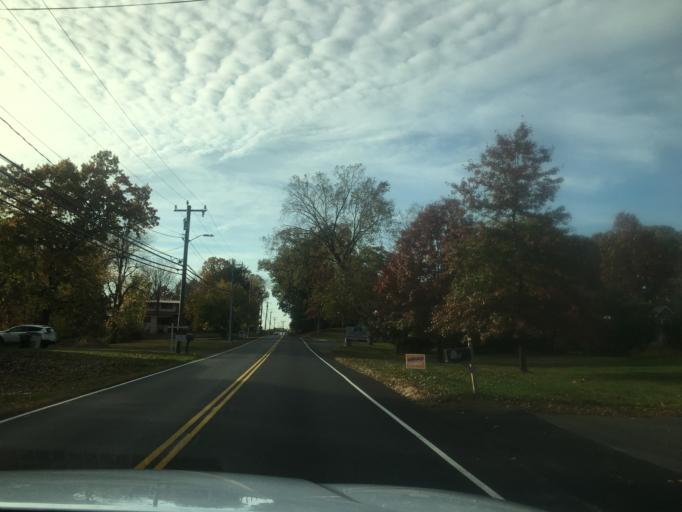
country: US
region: Connecticut
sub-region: Hartford County
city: South Windsor
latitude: 41.8176
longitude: -72.6031
